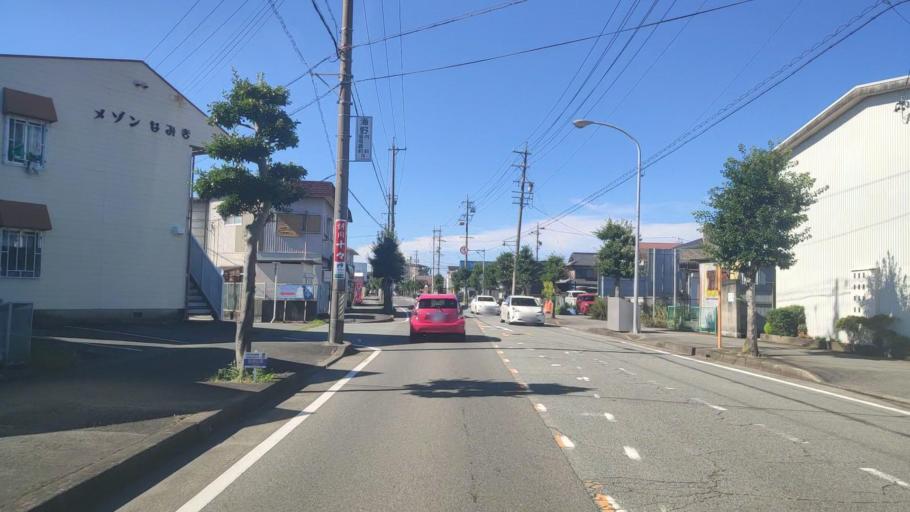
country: JP
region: Mie
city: Ise
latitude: 34.5001
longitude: 136.7073
